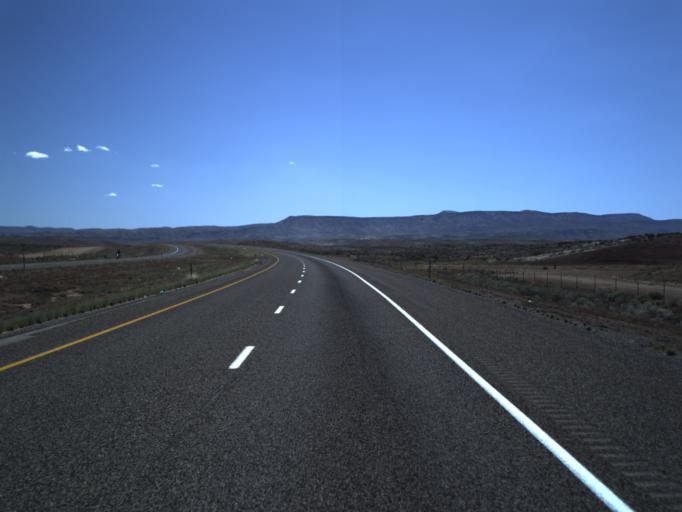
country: US
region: Utah
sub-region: Washington County
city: Saint George
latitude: 37.0097
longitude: -113.5900
